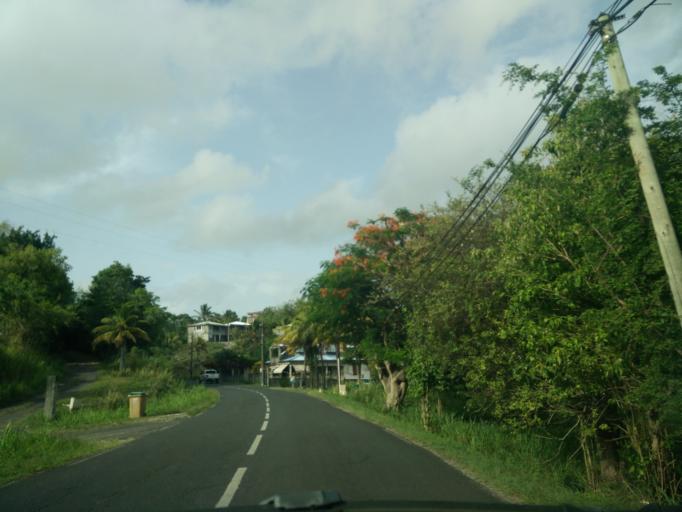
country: GP
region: Guadeloupe
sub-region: Guadeloupe
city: Sainte-Anne
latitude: 16.2669
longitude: -61.3739
